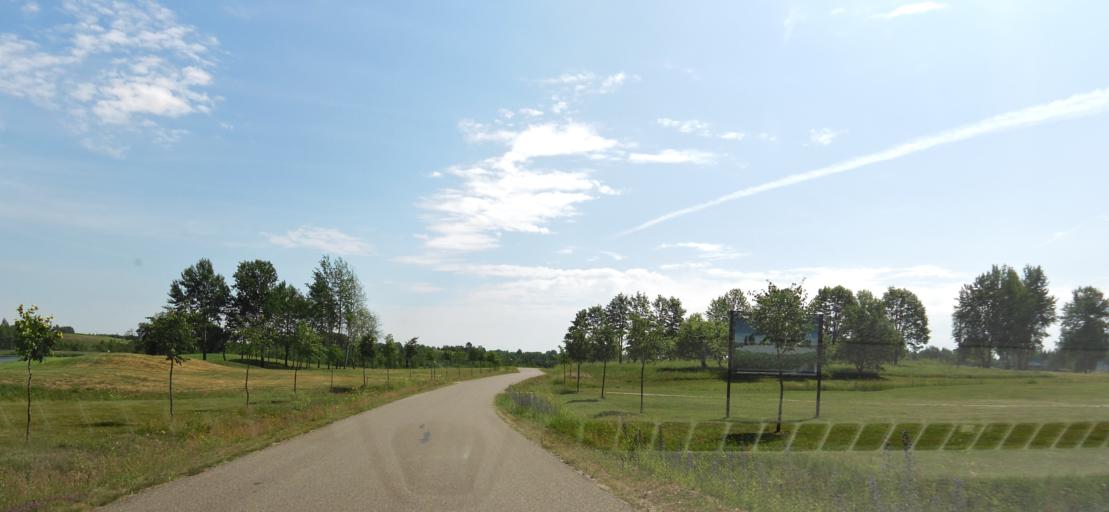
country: LT
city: Nemencine
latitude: 54.9107
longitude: 25.3133
